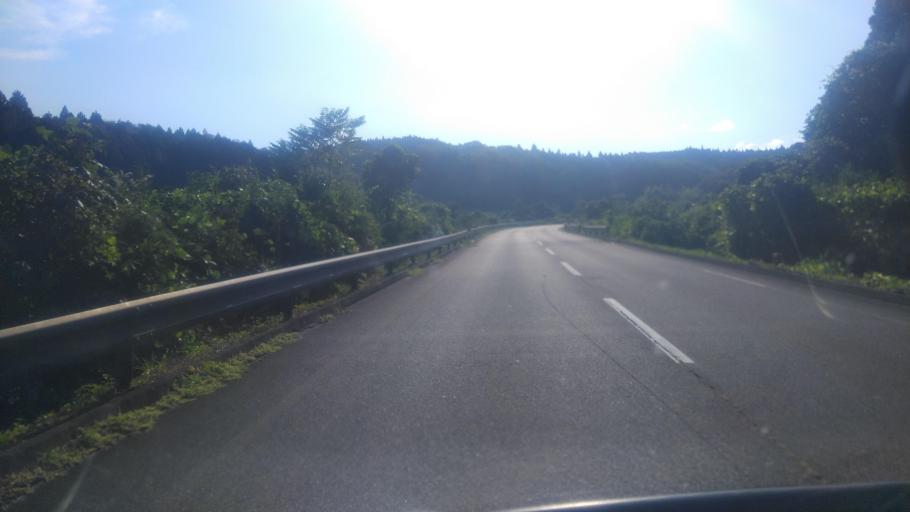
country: JP
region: Miyagi
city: Okawara
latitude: 38.0988
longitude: 140.7029
